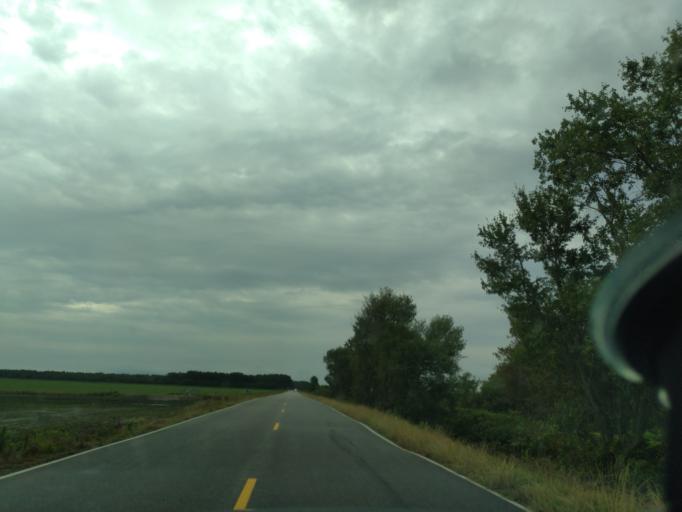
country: US
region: North Carolina
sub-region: Washington County
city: Plymouth
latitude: 35.8352
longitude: -76.5321
